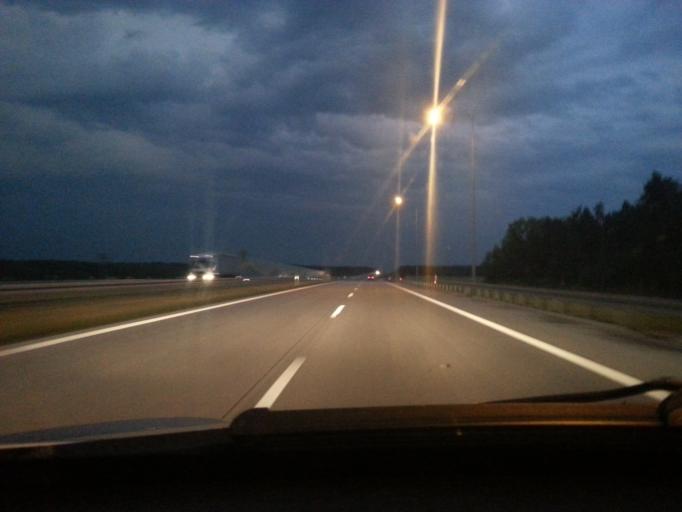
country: PL
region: Lodz Voivodeship
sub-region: Powiat sieradzki
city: Brzeznio
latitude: 51.5210
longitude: 18.6945
